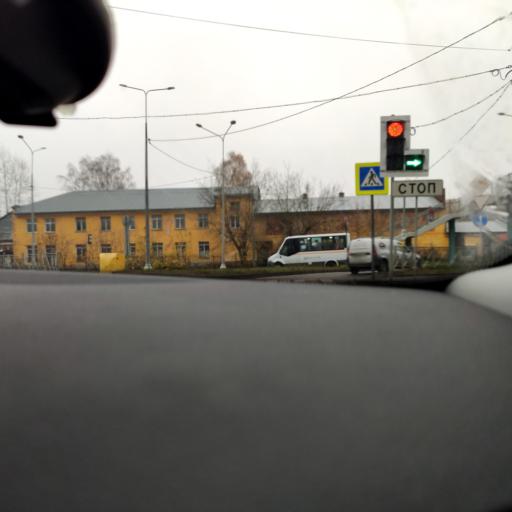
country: RU
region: Moskovskaya
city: Nakhabino
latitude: 55.8403
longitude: 37.1642
